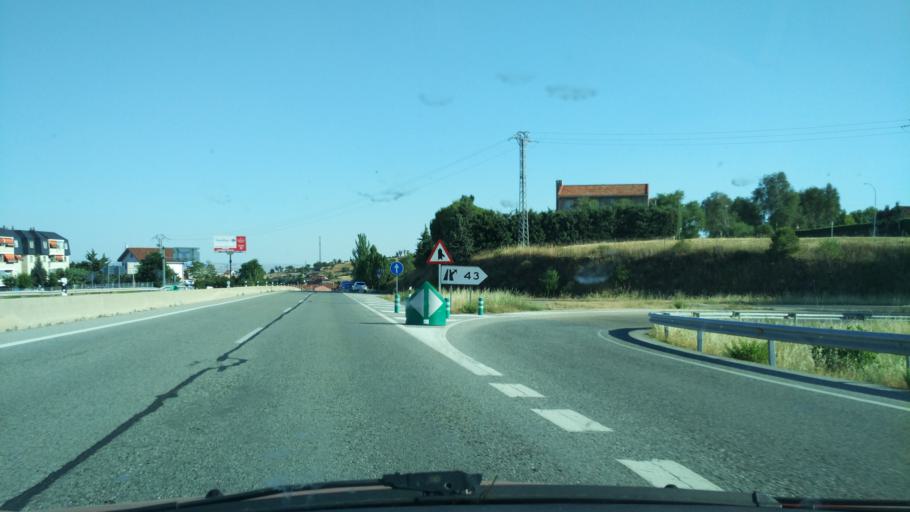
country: ES
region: Madrid
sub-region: Provincia de Madrid
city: El Molar
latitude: 40.7383
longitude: -3.5871
